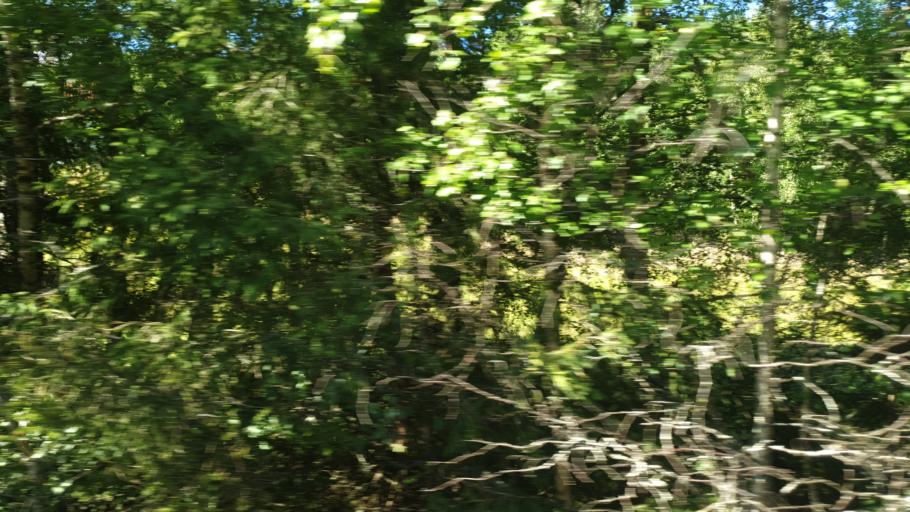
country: NO
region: Sor-Trondelag
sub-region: Meldal
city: Meldal
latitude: 63.1309
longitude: 9.7079
